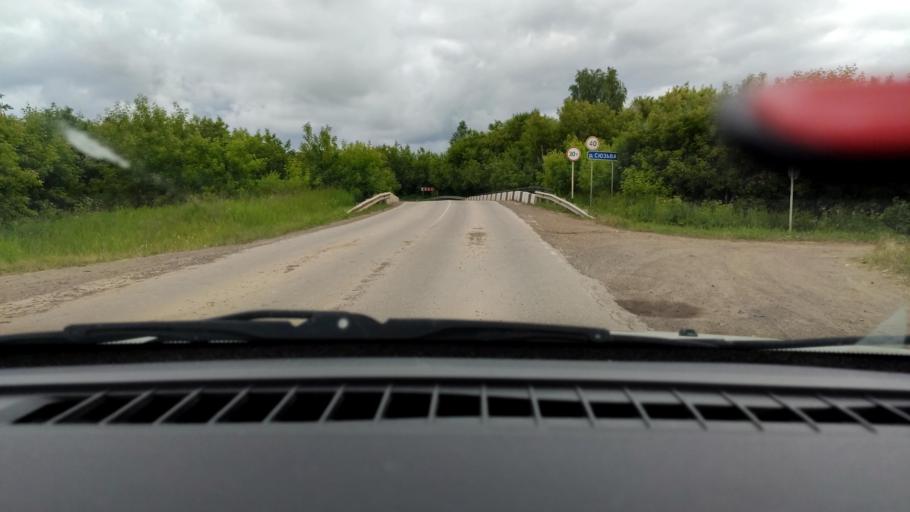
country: RU
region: Perm
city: Chaykovskaya
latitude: 58.1105
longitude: 55.5864
